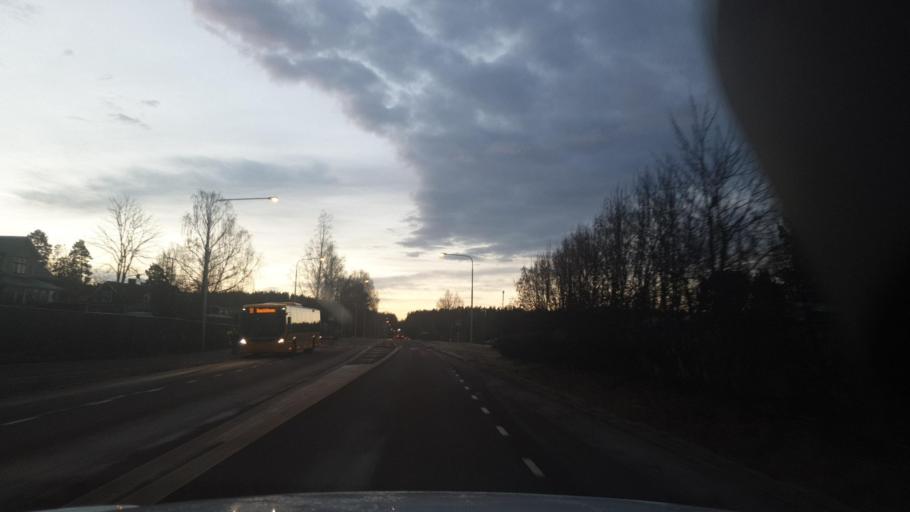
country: SE
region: Vaermland
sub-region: Arvika Kommun
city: Arvika
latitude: 59.6431
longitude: 12.6156
